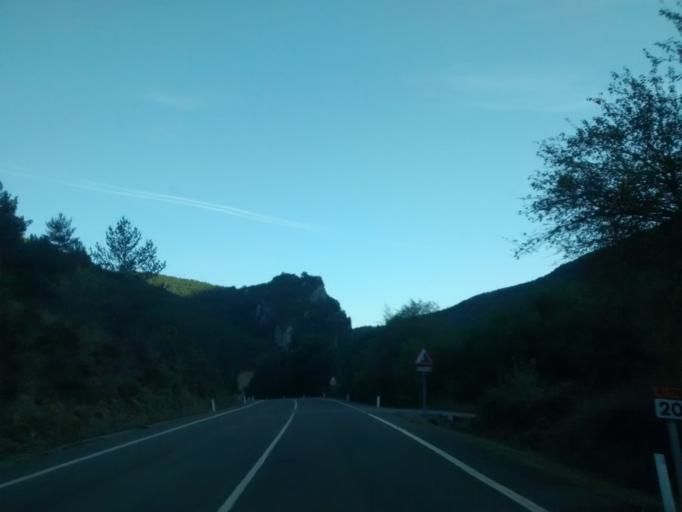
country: ES
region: Aragon
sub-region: Provincia de Huesca
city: Aragues del Puerto
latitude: 42.7066
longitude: -0.7494
